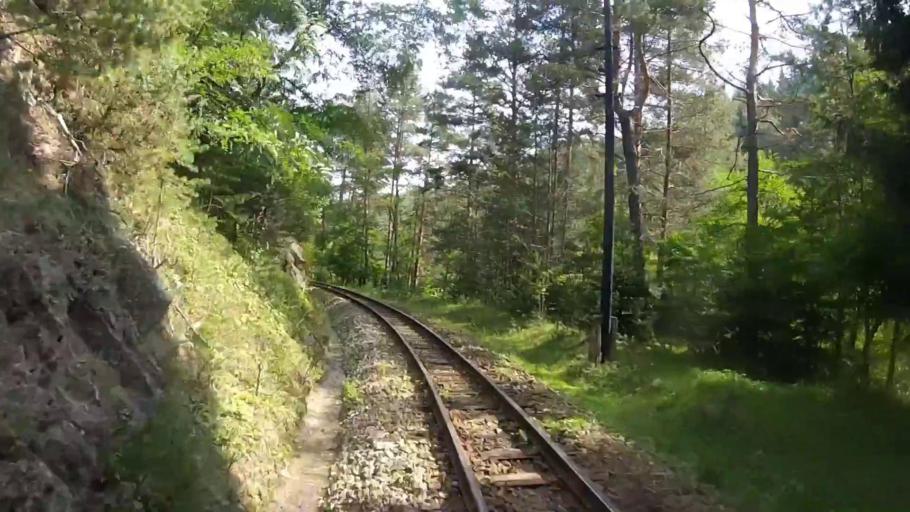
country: BG
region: Blagoevgrad
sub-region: Obshtina Yakoruda
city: Yakoruda
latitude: 42.0295
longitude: 23.7625
